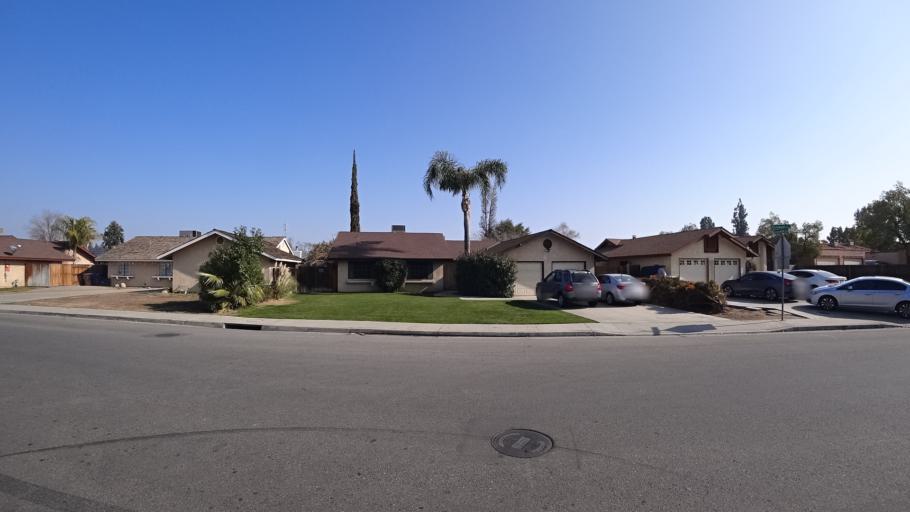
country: US
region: California
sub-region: Kern County
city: Bakersfield
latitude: 35.3188
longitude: -119.0514
